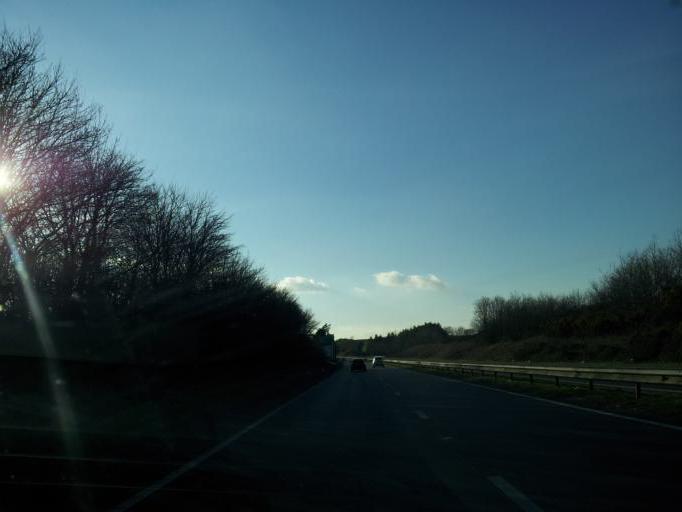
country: GB
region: England
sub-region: Devon
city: Okehampton
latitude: 50.7181
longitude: -3.8299
